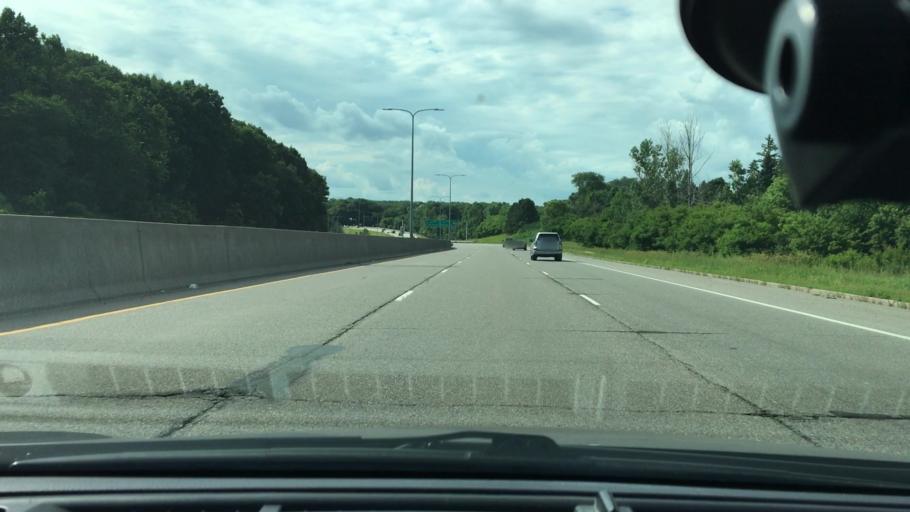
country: US
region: Minnesota
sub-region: Hennepin County
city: Wayzata
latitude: 44.9732
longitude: -93.4955
